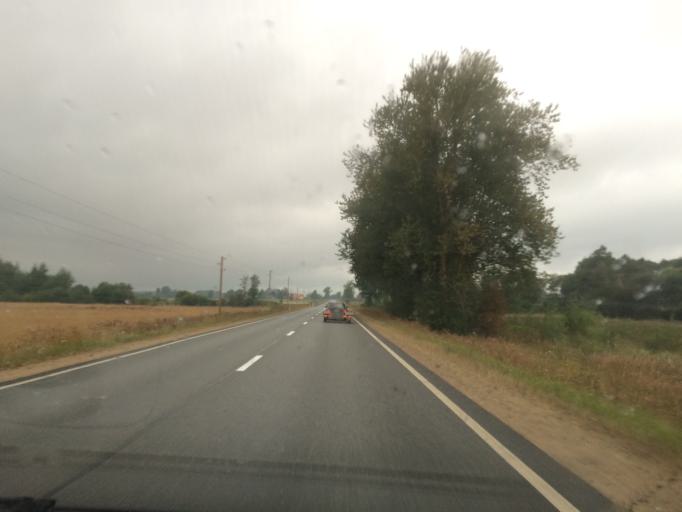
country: LV
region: Livani
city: Livani
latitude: 56.5324
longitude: 26.3367
